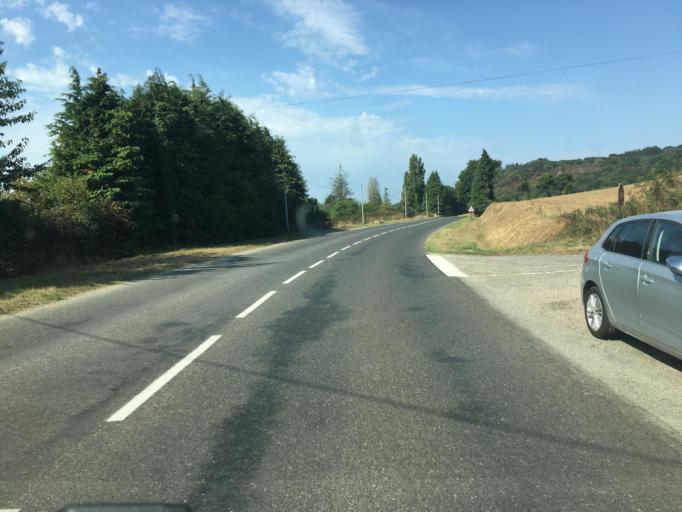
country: FR
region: Brittany
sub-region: Departement des Cotes-d'Armor
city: Mur-de-Bretagne
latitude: 48.2173
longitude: -3.0171
